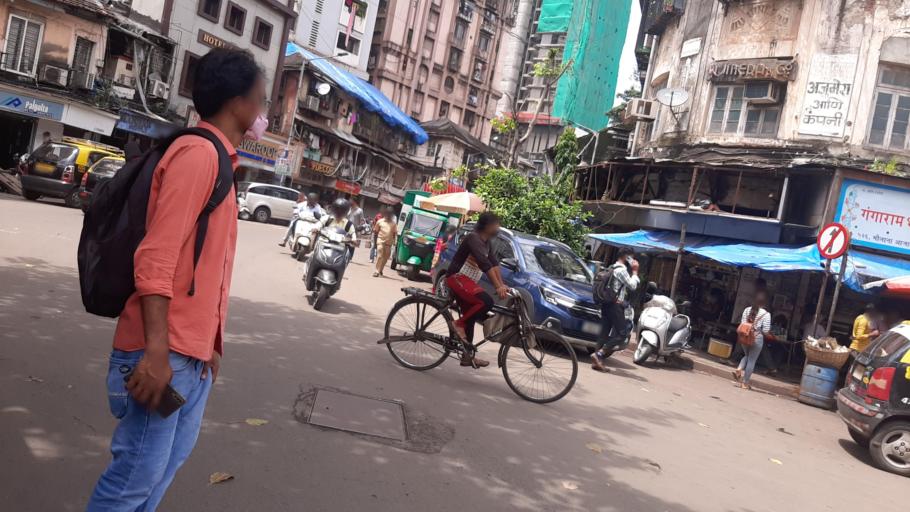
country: IN
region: Maharashtra
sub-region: Mumbai Suburban
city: Mumbai
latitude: 18.9567
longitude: 72.8285
